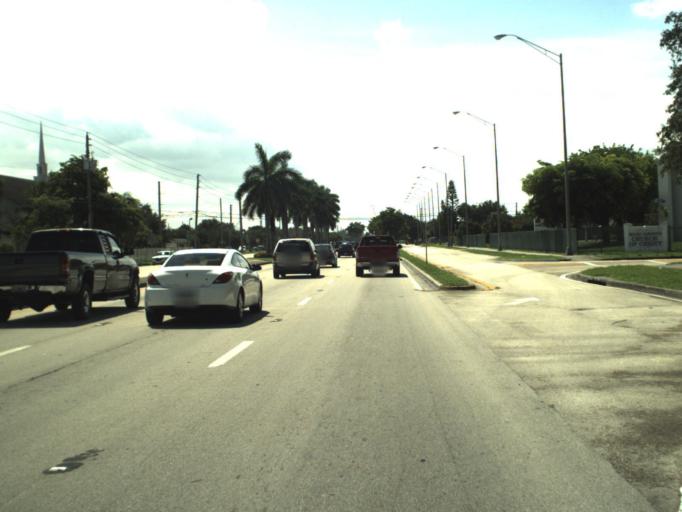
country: US
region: Florida
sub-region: Miami-Dade County
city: Scott Lake
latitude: 25.9414
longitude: -80.2377
